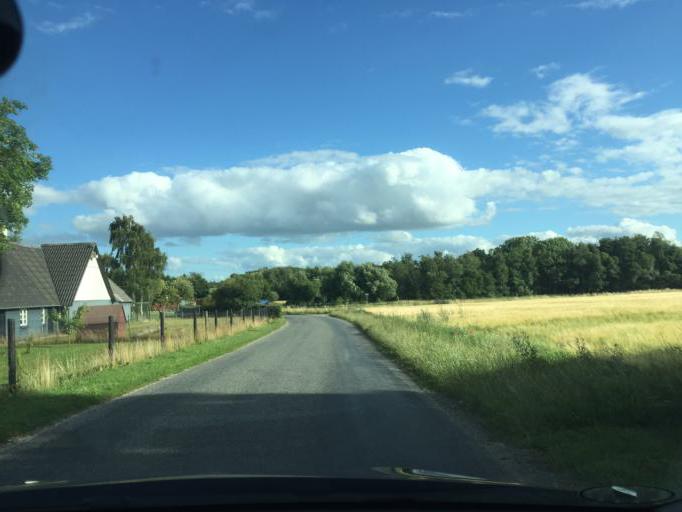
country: DK
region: South Denmark
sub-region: Faaborg-Midtfyn Kommune
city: Arslev
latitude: 55.2966
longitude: 10.5344
